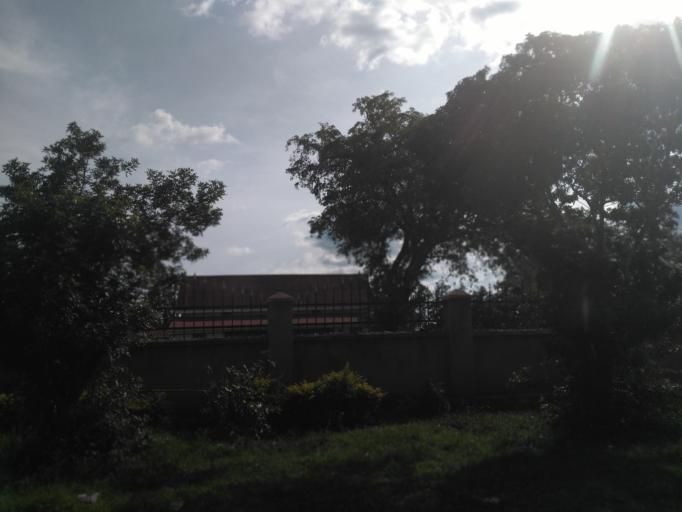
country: UG
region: Eastern Region
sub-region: Jinja District
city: Jinja
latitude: 0.4204
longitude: 33.2015
